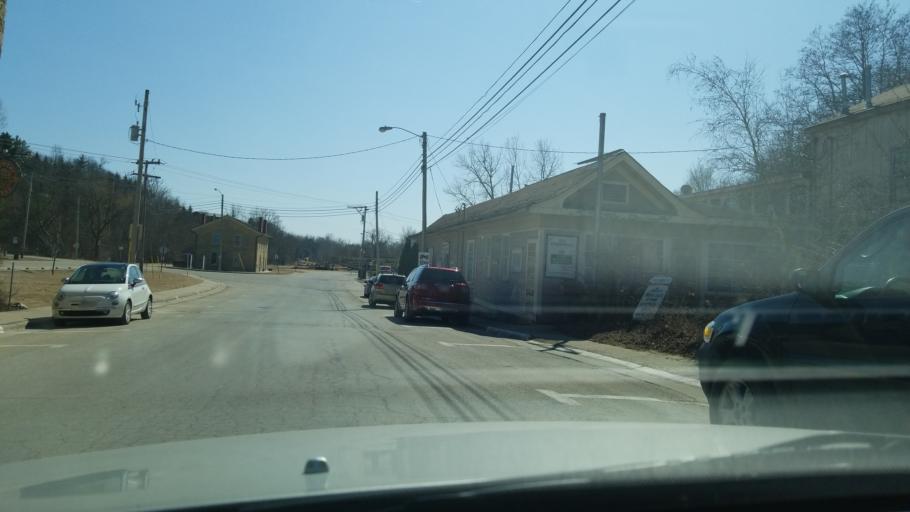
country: US
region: Wisconsin
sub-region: Iowa County
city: Mineral Point
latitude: 42.8578
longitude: -90.1770
